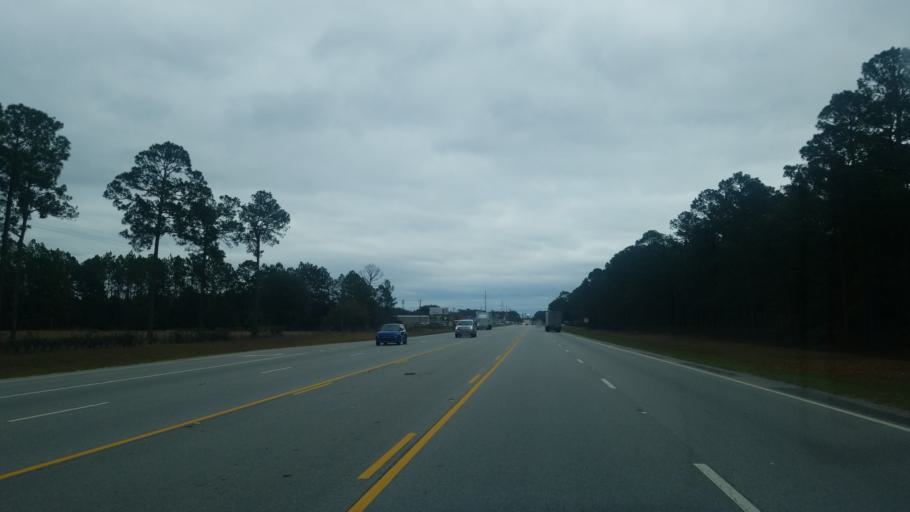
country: US
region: Georgia
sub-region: Ware County
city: Deenwood
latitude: 31.2088
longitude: -82.3940
